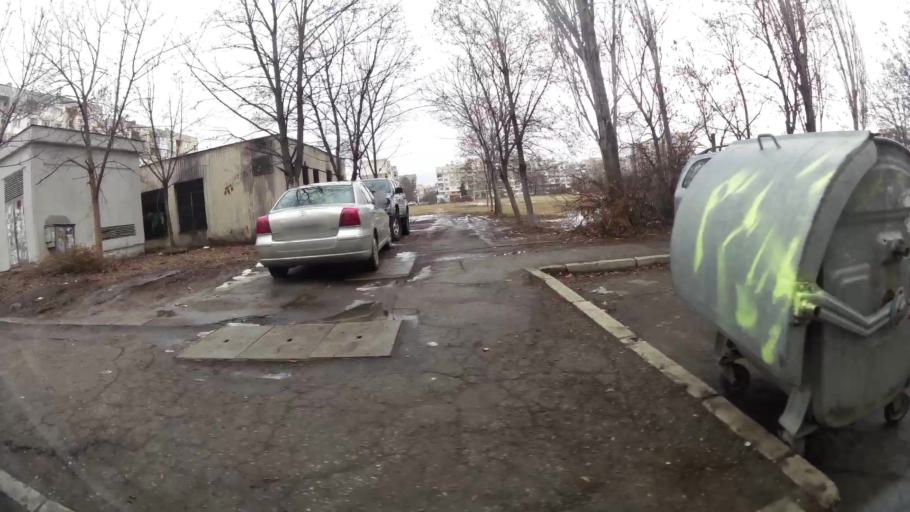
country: BG
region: Sofiya
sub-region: Obshtina Bozhurishte
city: Bozhurishte
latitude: 42.7268
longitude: 23.2547
